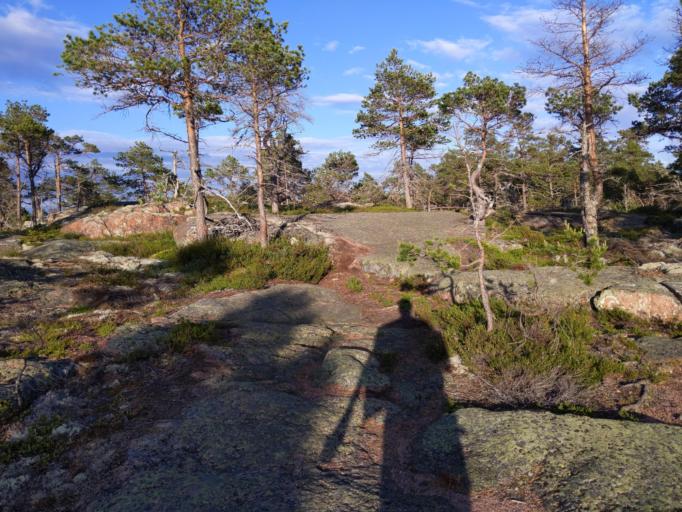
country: SE
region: Vaesternorrland
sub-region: OErnskoeldsviks Kommun
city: Ornskoldsvik
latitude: 63.1673
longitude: 18.7163
